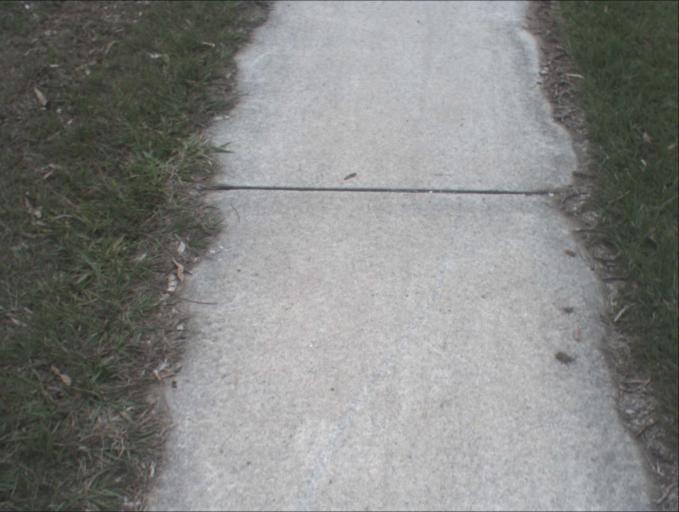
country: AU
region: Queensland
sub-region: Logan
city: North Maclean
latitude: -27.7483
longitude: 153.0146
